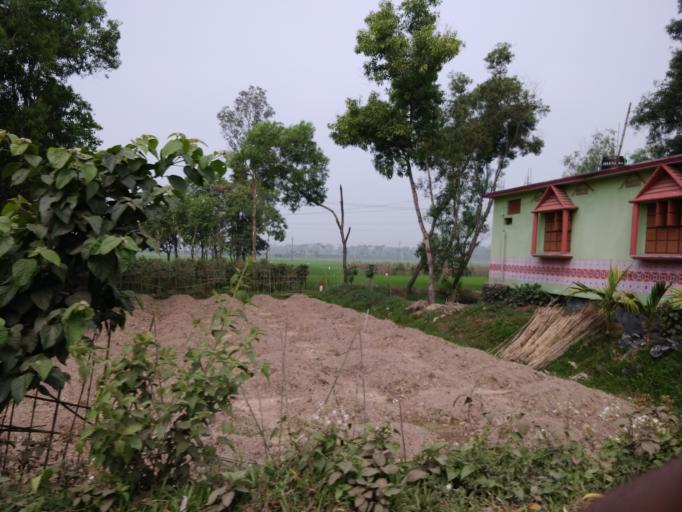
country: BD
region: Sylhet
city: Habiganj
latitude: 24.1643
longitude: 91.3535
